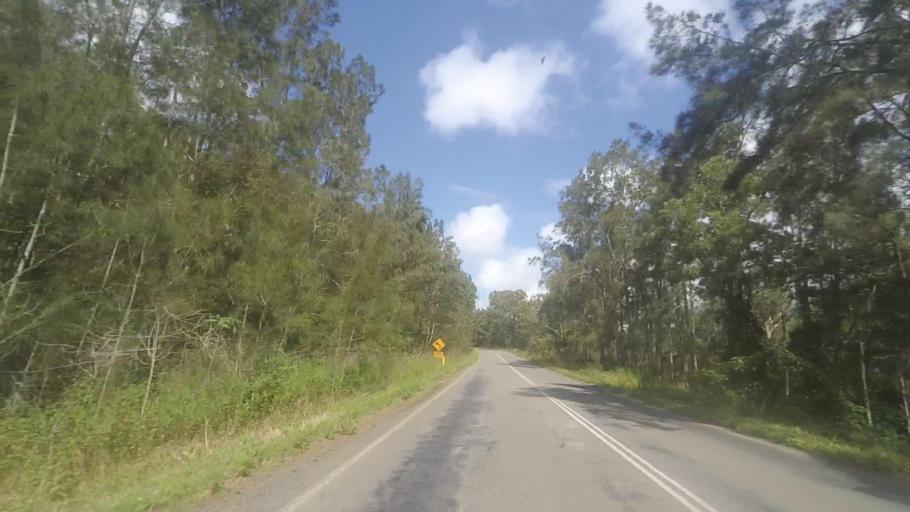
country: AU
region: New South Wales
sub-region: Great Lakes
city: Bulahdelah
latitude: -32.3908
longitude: 152.4308
